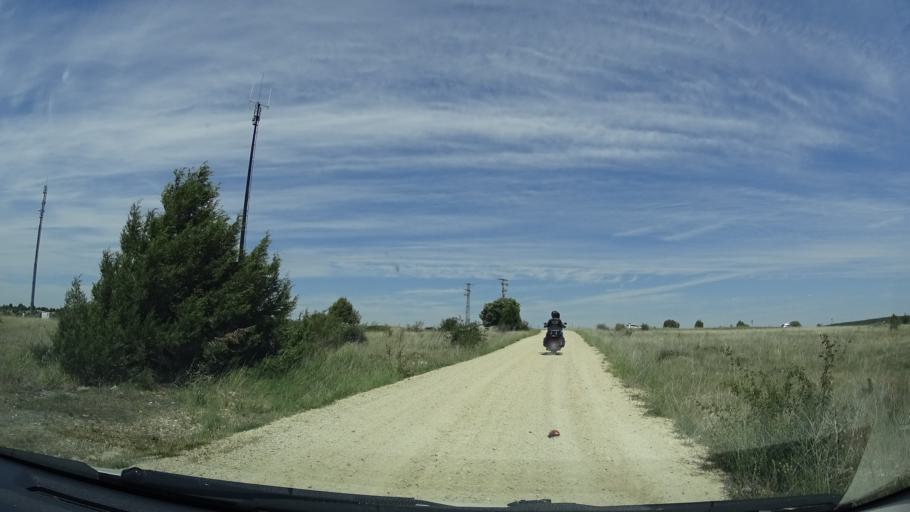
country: ES
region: Castille and Leon
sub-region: Provincia de Segovia
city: Pradena
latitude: 41.1445
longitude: -3.6783
